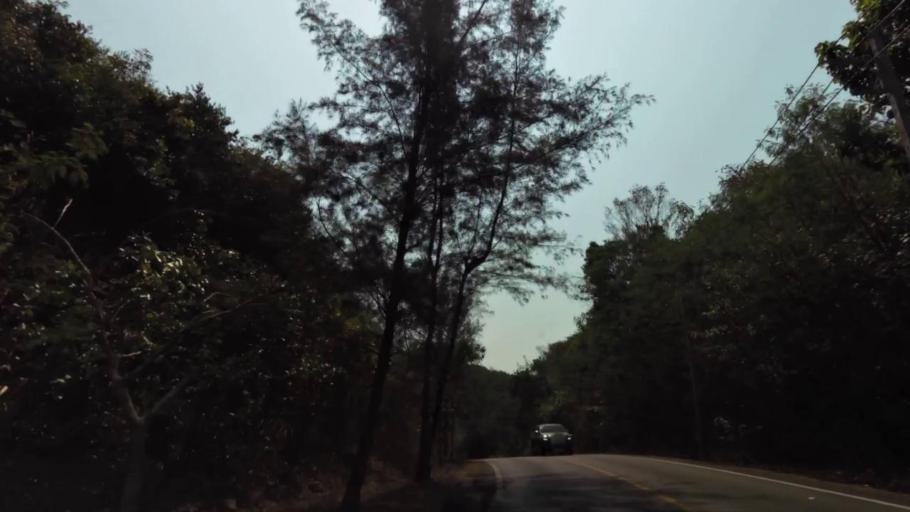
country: TH
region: Chanthaburi
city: Tha Mai
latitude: 12.5258
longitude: 101.9474
